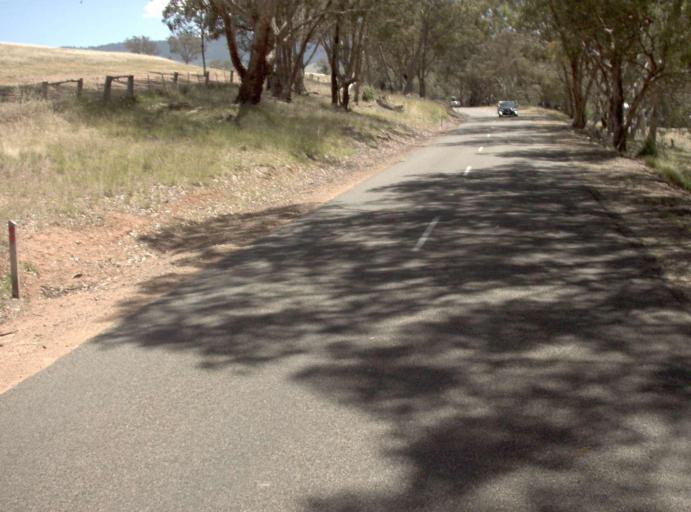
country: AU
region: Victoria
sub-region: East Gippsland
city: Bairnsdale
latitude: -37.2154
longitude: 147.7169
